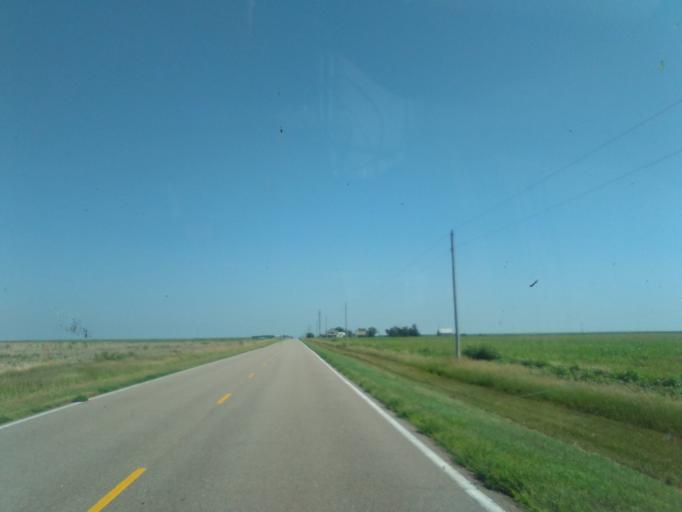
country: US
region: Nebraska
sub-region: Dundy County
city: Benkelman
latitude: 39.8108
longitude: -101.5416
